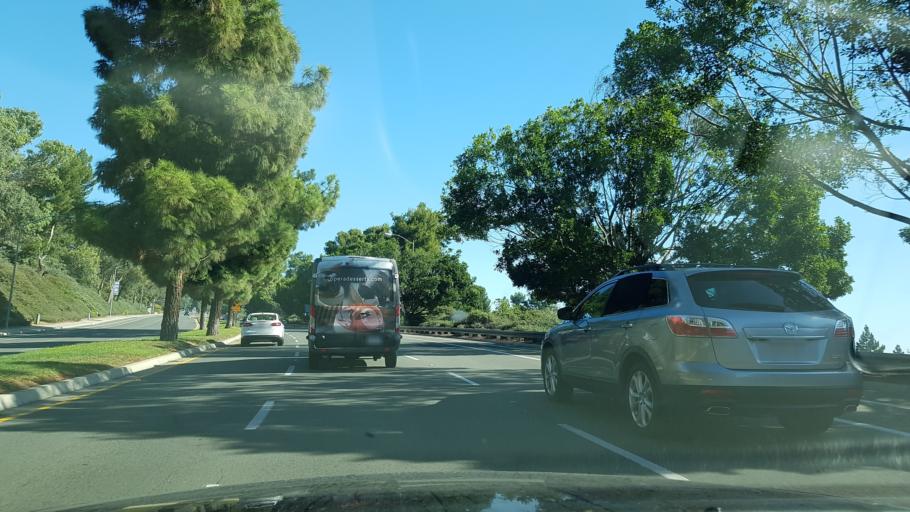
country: US
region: California
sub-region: San Diego County
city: La Jolla
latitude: 32.8936
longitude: -117.1954
